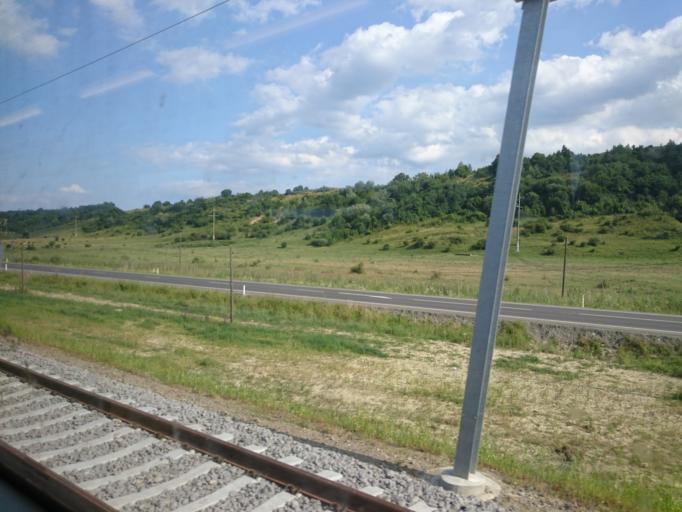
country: RO
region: Sibiu
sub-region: Comuna Hoghilag
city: Hoghilag
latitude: 46.2200
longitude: 24.6101
